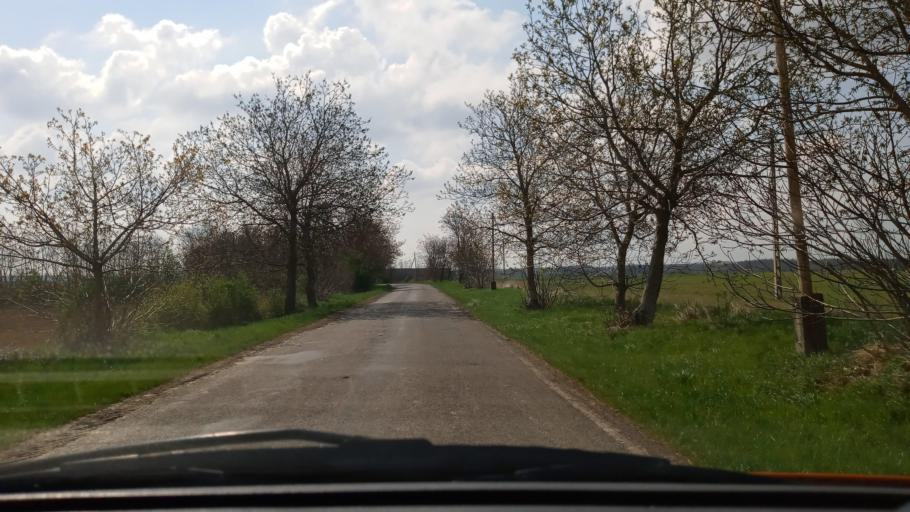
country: HU
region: Baranya
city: Pecsvarad
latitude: 46.0852
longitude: 18.5056
